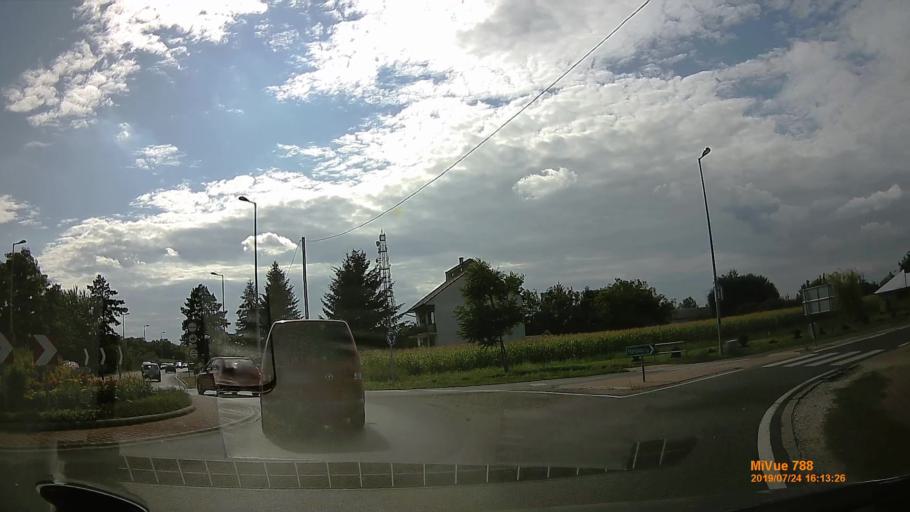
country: HU
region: Szabolcs-Szatmar-Bereg
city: Nyirpazony
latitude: 47.9498
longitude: 21.8043
